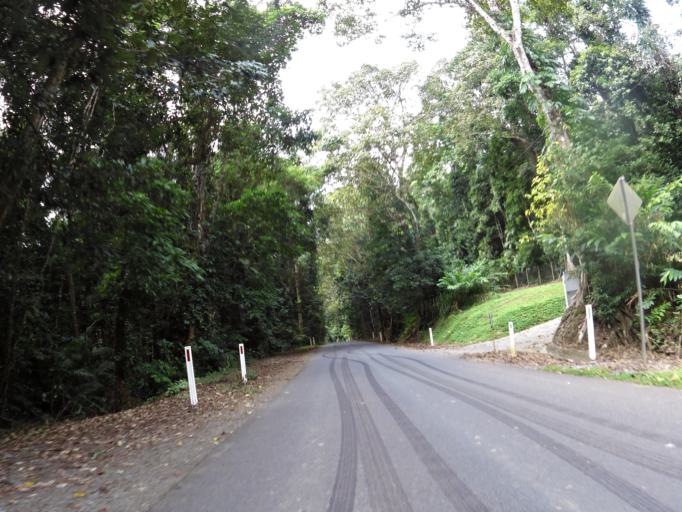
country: AU
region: Queensland
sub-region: Cairns
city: Woree
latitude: -16.9615
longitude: 145.6804
